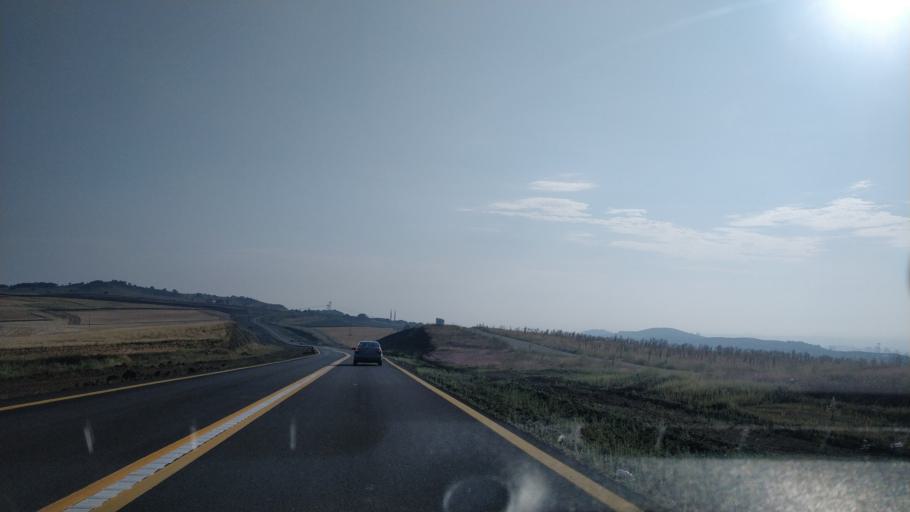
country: TR
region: Ankara
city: Etimesgut
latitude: 39.8560
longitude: 32.5674
